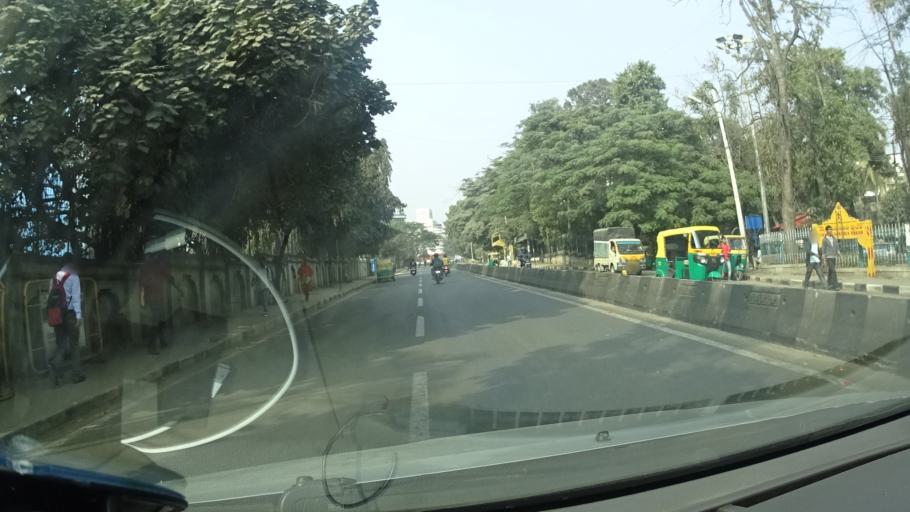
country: IN
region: Karnataka
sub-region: Bangalore Urban
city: Bangalore
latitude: 12.9843
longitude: 77.5996
